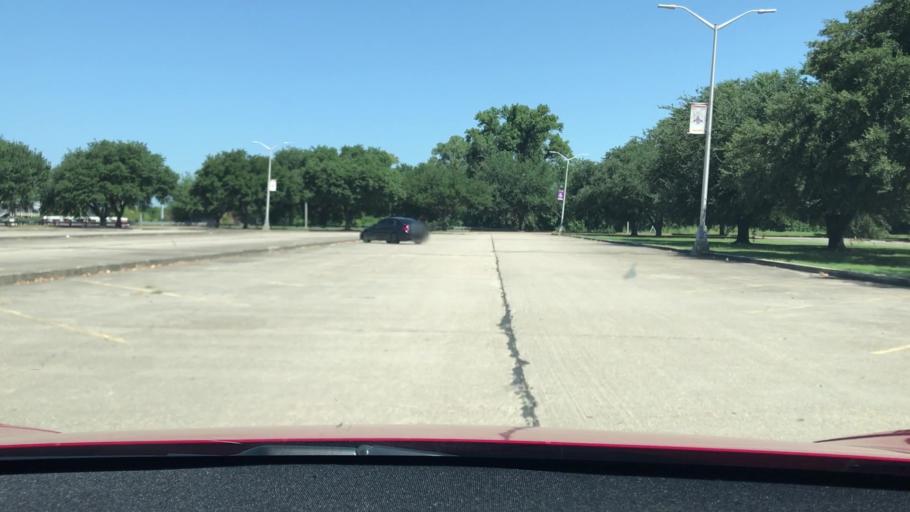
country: US
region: Louisiana
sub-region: Bossier Parish
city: Bossier City
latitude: 32.4304
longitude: -93.7050
